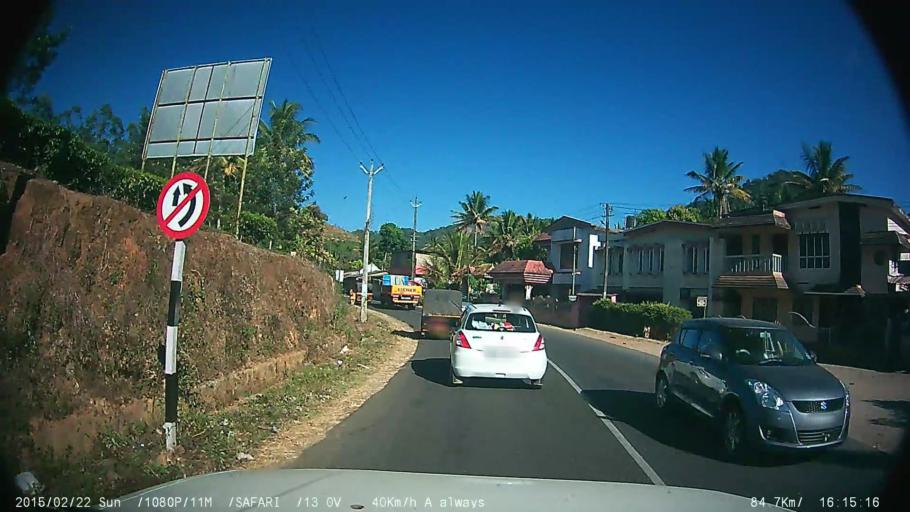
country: IN
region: Tamil Nadu
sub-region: Theni
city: Gudalur
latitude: 9.5842
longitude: 77.1056
